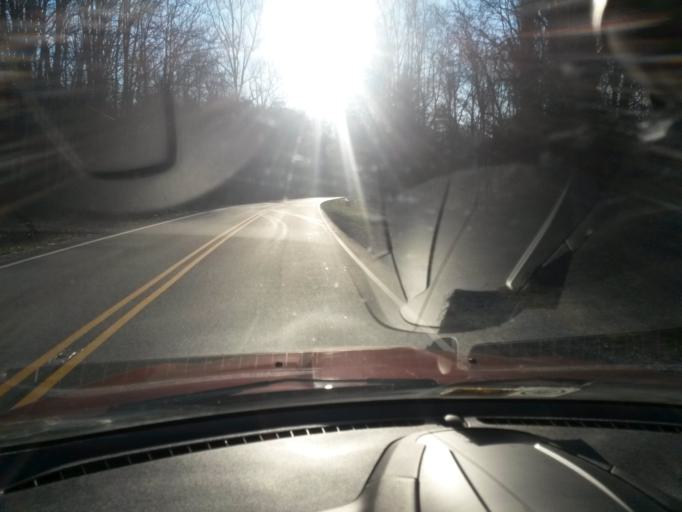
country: US
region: Virginia
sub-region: Amherst County
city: Amherst
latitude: 37.6187
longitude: -79.0938
